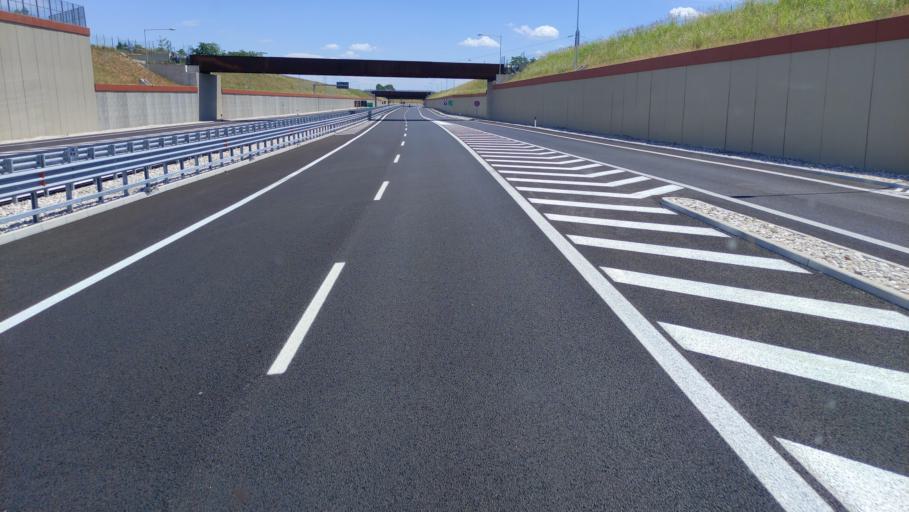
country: IT
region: Veneto
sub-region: Provincia di Treviso
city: Caselle
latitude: 45.7302
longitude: 11.9704
